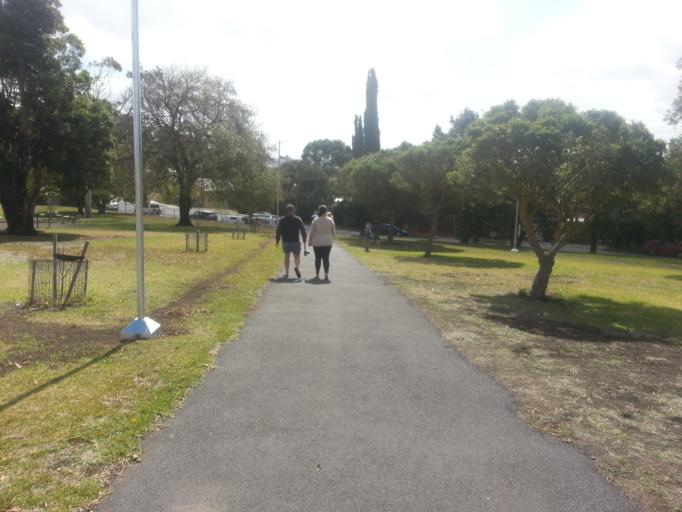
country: AU
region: South Australia
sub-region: Mount Gambier
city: Mount Gambier
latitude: -37.8436
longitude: 140.7786
